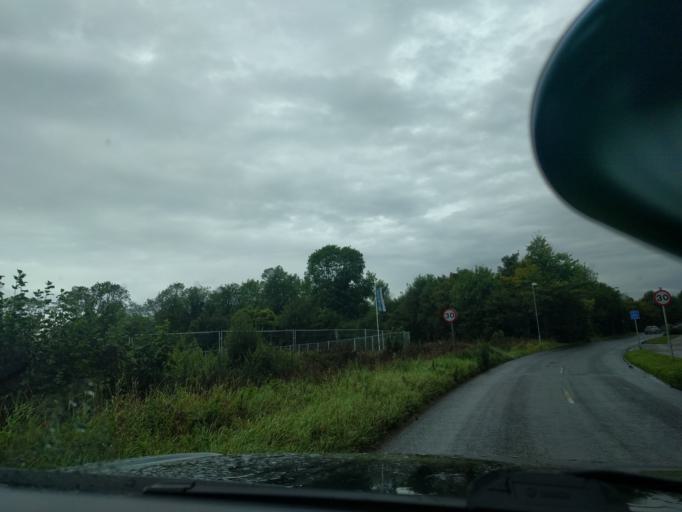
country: GB
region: England
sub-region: Wiltshire
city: Neston
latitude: 51.4297
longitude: -2.2099
